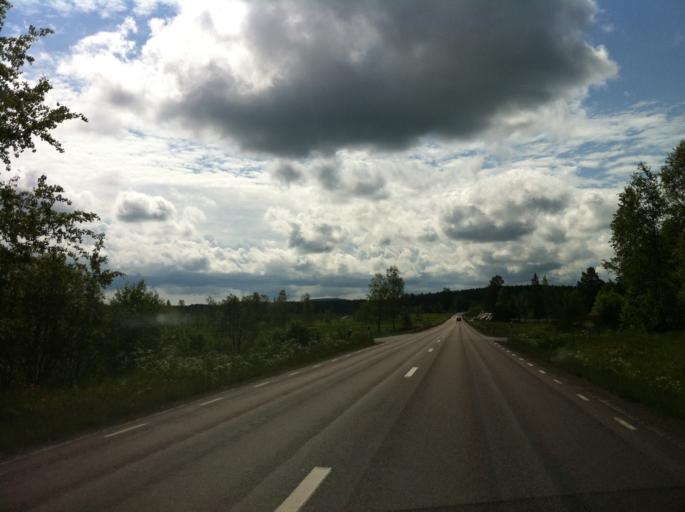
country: SE
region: Vaermland
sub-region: Karlstads Kommun
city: Edsvalla
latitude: 59.6044
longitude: 13.1584
